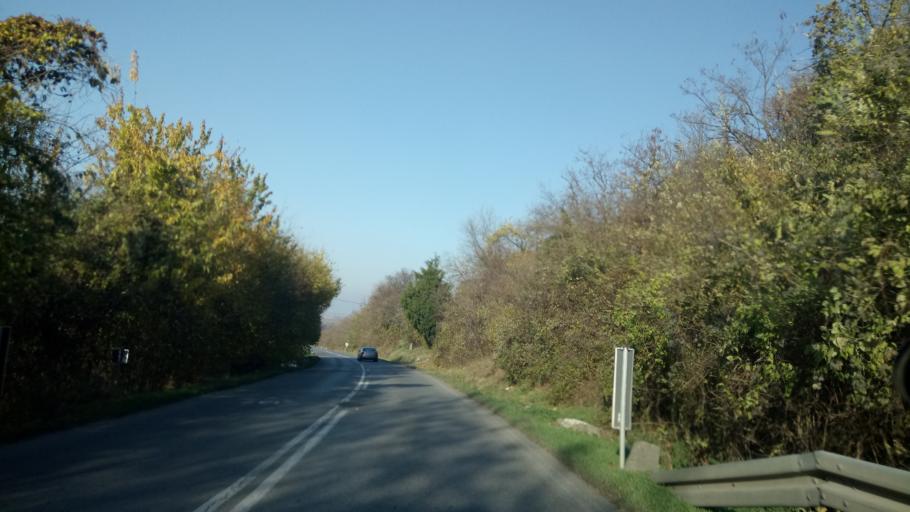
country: RS
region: Autonomna Pokrajina Vojvodina
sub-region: Juznobacki Okrug
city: Sremski Karlovci
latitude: 45.1804
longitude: 19.9532
